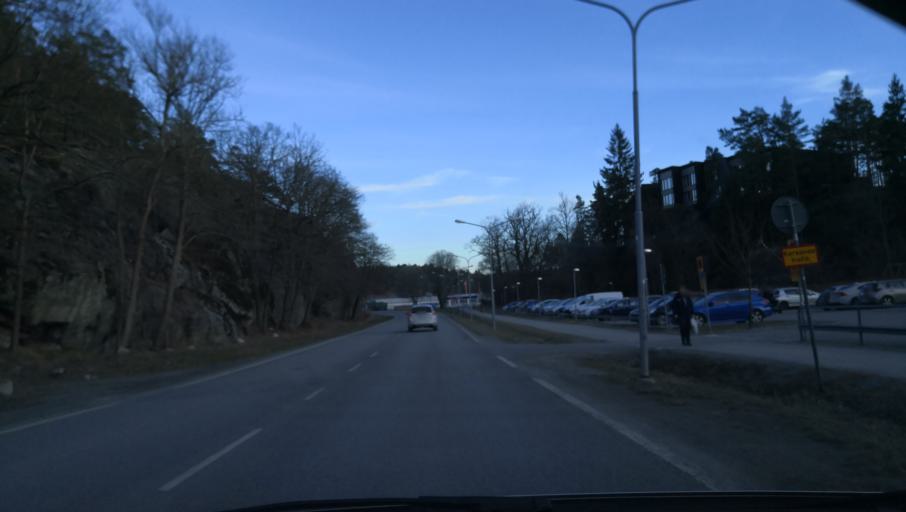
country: SE
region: Stockholm
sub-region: Varmdo Kommun
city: Gustavsberg
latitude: 59.3312
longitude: 18.3896
